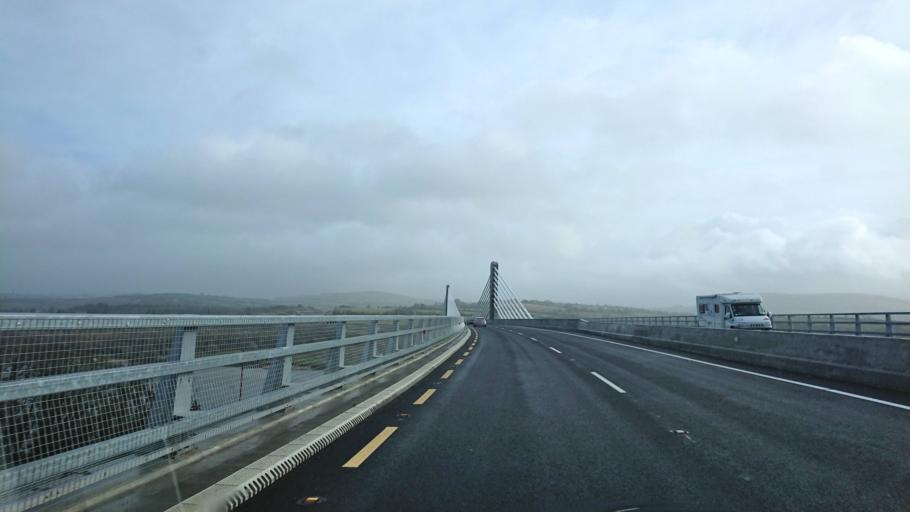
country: IE
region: Leinster
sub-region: Loch Garman
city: New Ross
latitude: 52.3568
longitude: -6.9978
